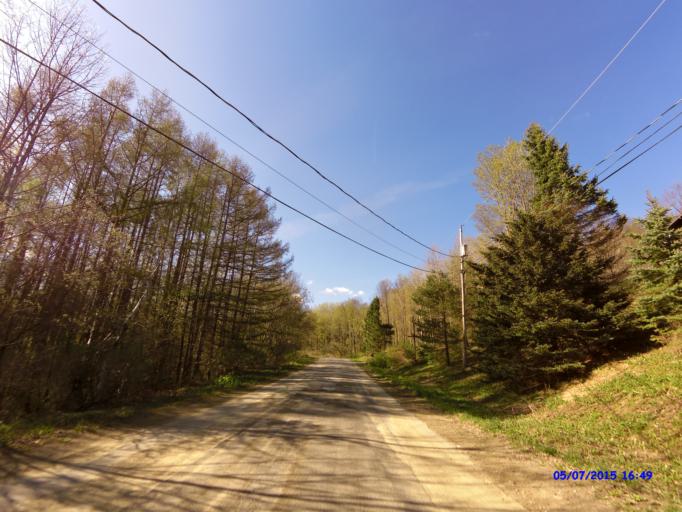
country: US
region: New York
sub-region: Cattaraugus County
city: Little Valley
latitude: 42.2835
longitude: -78.6994
